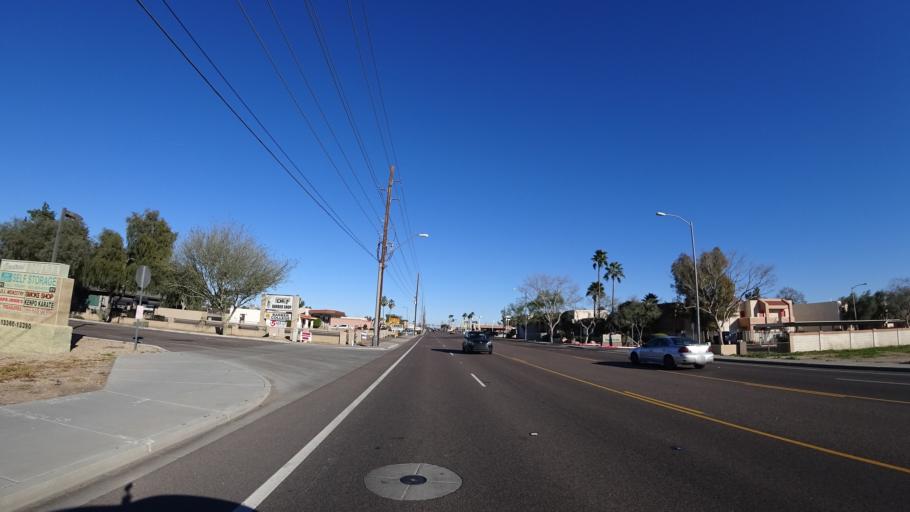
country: US
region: Arizona
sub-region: Maricopa County
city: Avondale
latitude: 33.4499
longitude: -112.3466
